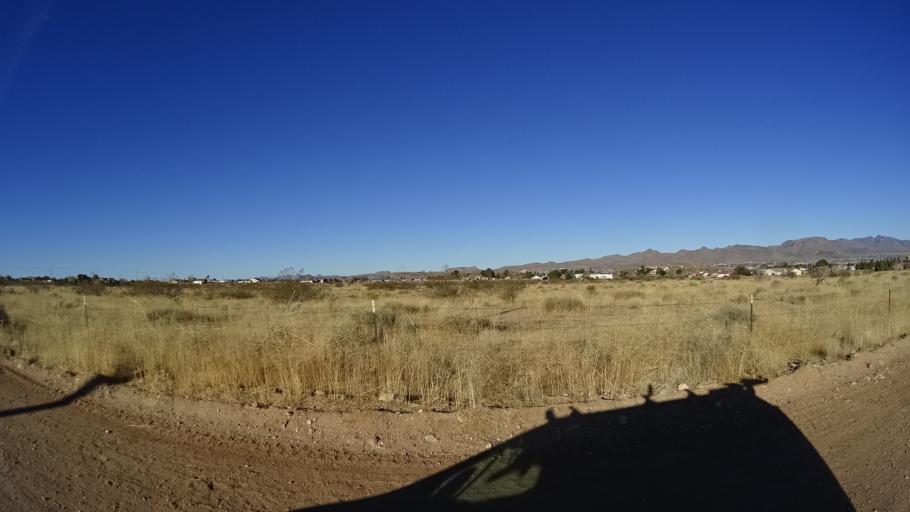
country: US
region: Arizona
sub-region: Mohave County
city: Kingman
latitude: 35.2021
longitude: -113.9938
